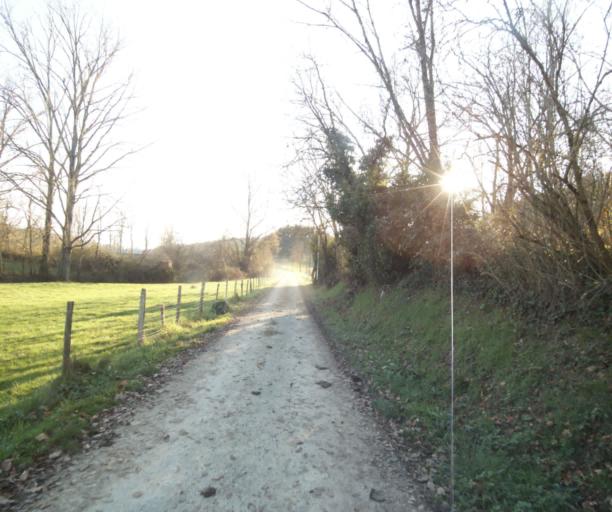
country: FR
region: Midi-Pyrenees
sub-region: Departement du Tarn-et-Garonne
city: Moissac
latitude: 44.1397
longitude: 1.1303
